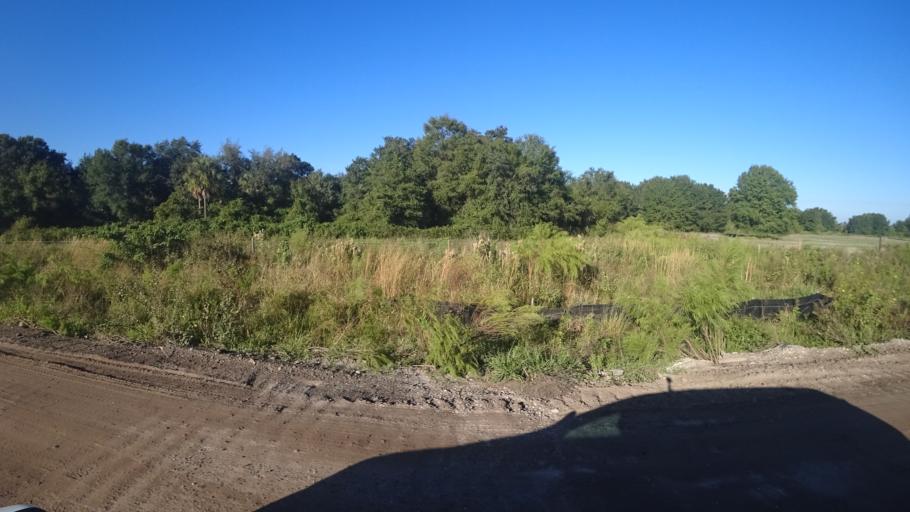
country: US
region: Florida
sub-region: Hillsborough County
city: Ruskin
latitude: 27.6277
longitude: -82.4884
